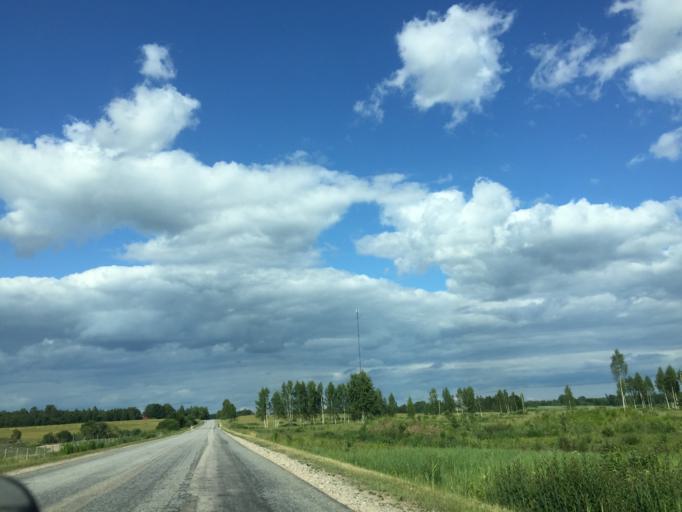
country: LV
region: Ogre
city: Jumprava
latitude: 56.7864
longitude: 25.0255
